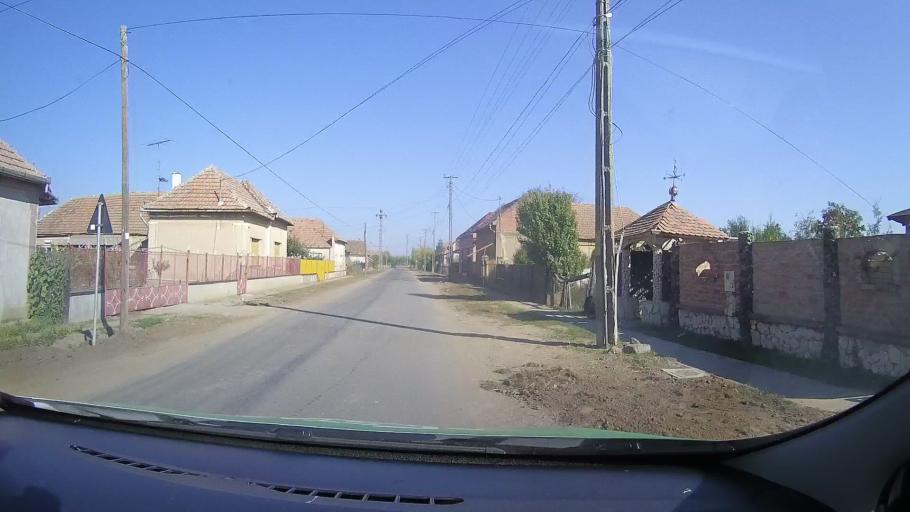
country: RO
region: Satu Mare
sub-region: Comuna Ciumesti
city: Ciumesti
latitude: 47.6678
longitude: 22.3383
